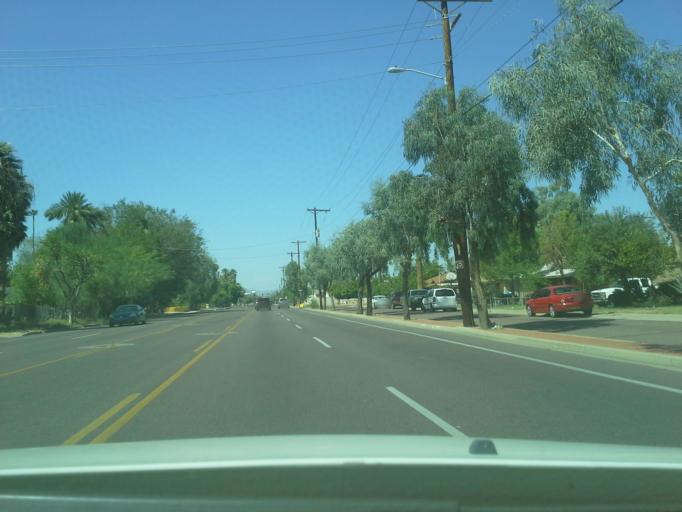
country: US
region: Arizona
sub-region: Maricopa County
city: Phoenix
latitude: 33.3811
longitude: -112.0646
